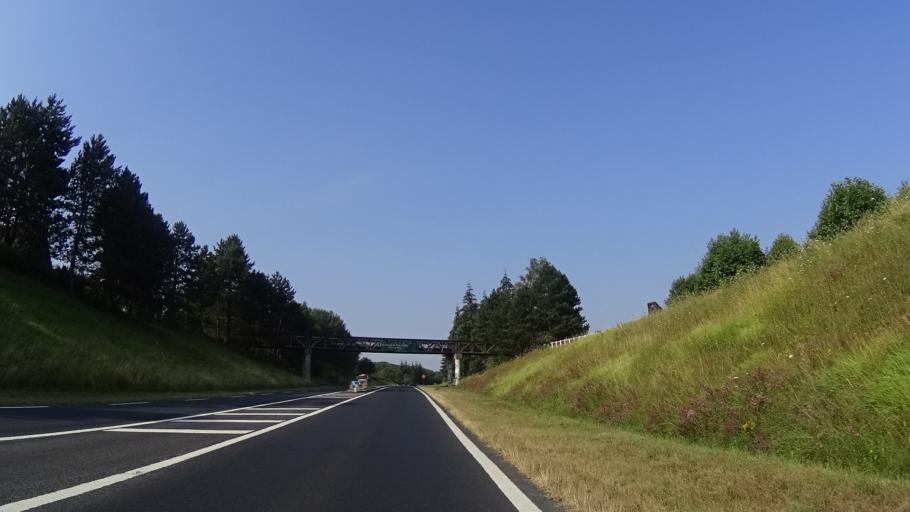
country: FR
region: Ile-de-France
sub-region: Departement du Val-d'Oise
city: Seugy
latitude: 49.1155
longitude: 2.4017
